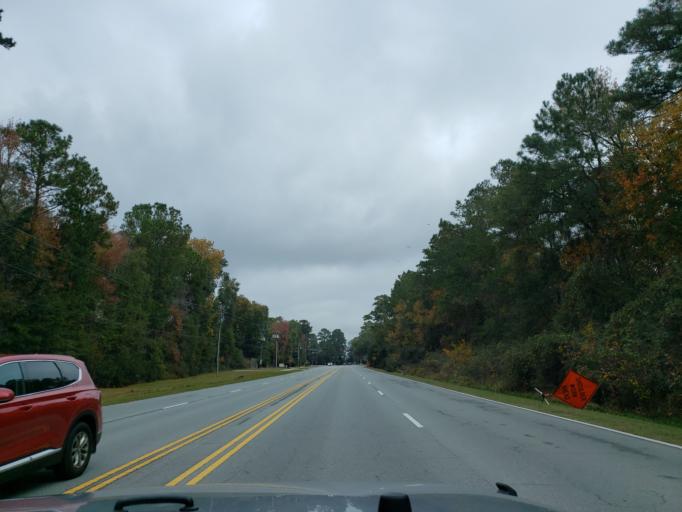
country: US
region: Georgia
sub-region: Chatham County
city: Whitemarsh Island
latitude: 32.0336
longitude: -80.9922
